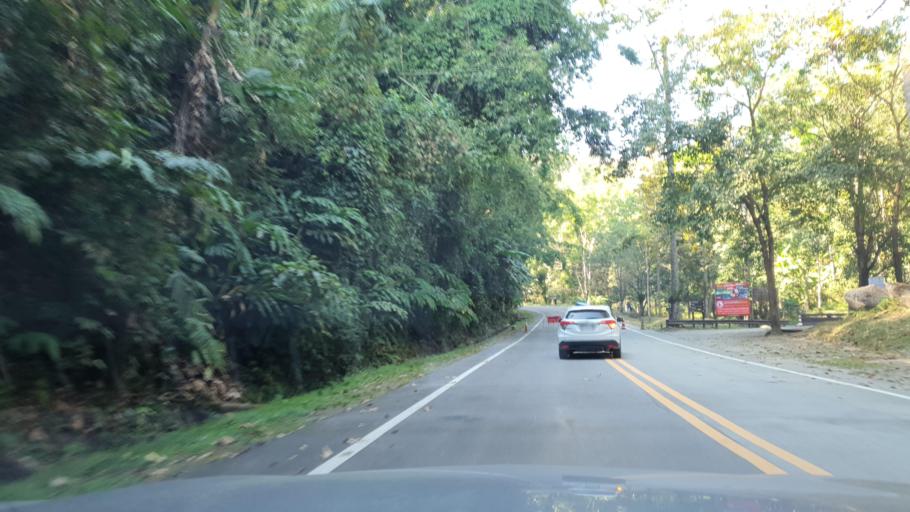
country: TH
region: Chiang Rai
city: Mae Lao
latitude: 19.8754
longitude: 99.6263
